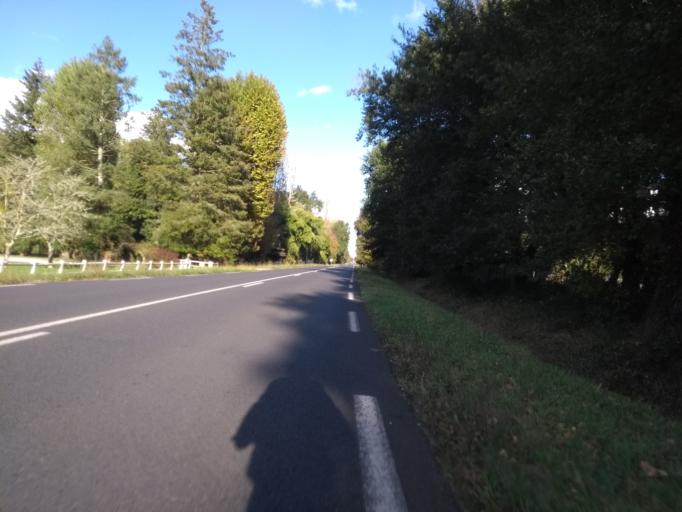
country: FR
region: Aquitaine
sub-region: Departement de la Gironde
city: Cestas
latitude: 44.7227
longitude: -0.6846
